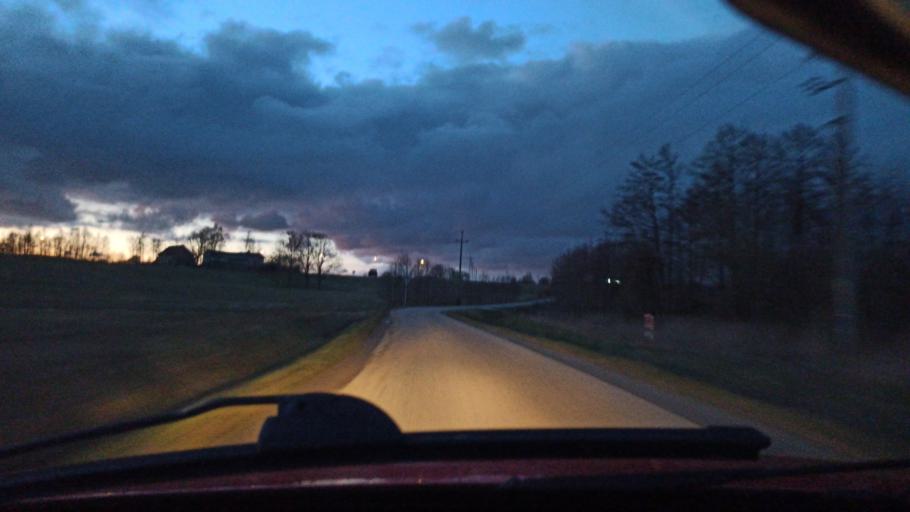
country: PL
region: Warmian-Masurian Voivodeship
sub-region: Powiat elblaski
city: Gronowo Gorne
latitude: 54.1680
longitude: 19.5357
